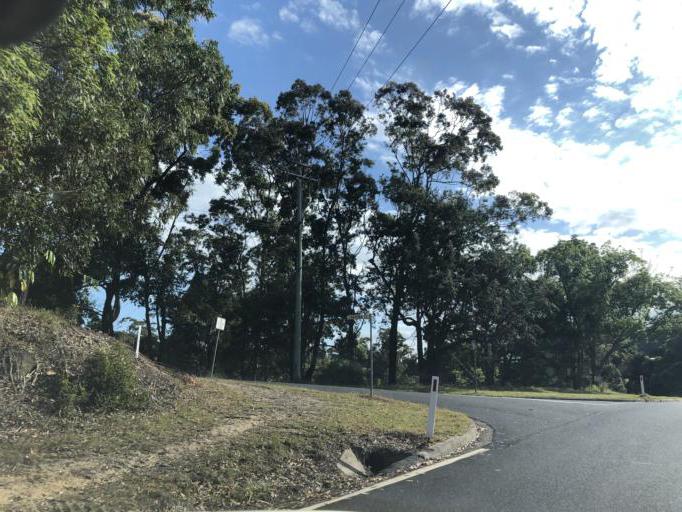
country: AU
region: New South Wales
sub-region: Coffs Harbour
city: Coffs Harbour
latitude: -30.2613
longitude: 153.1321
